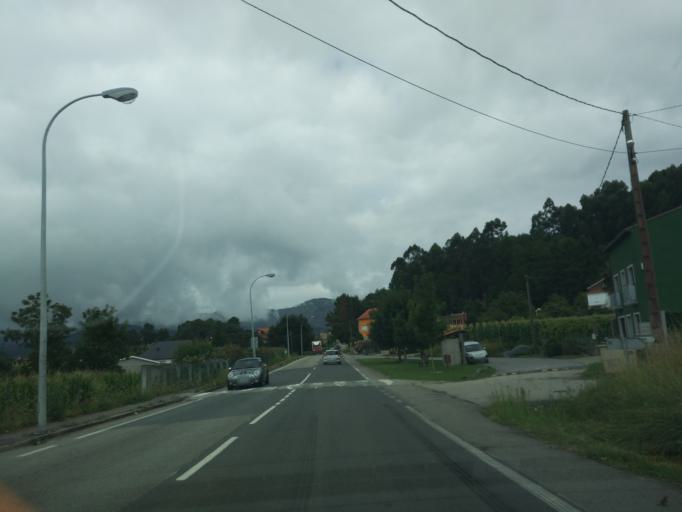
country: ES
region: Galicia
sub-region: Provincia da Coruna
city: Boiro
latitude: 42.6426
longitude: -8.8678
